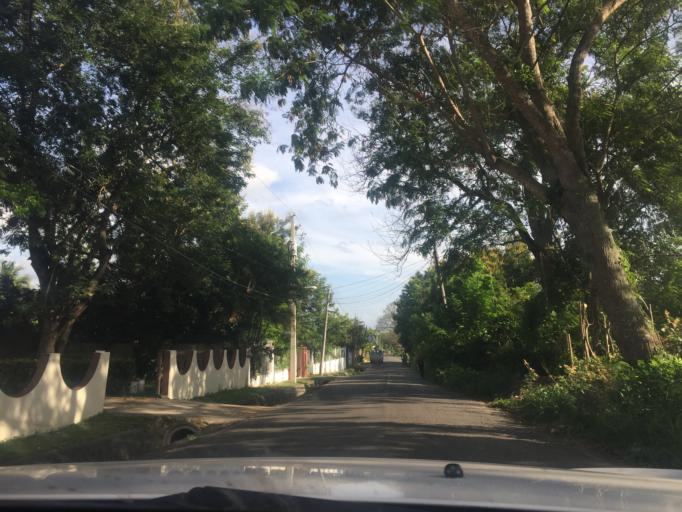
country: DO
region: Santiago
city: Tamboril
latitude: 19.4863
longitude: -70.6369
